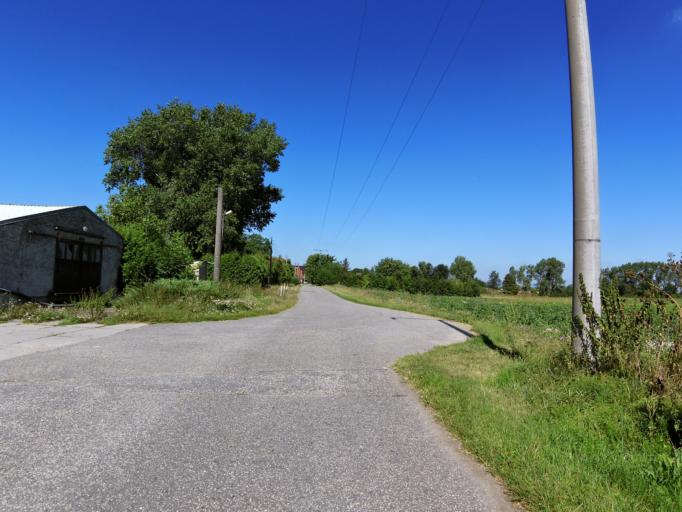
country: DE
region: Brandenburg
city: Muhlberg
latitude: 51.4058
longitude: 13.2228
